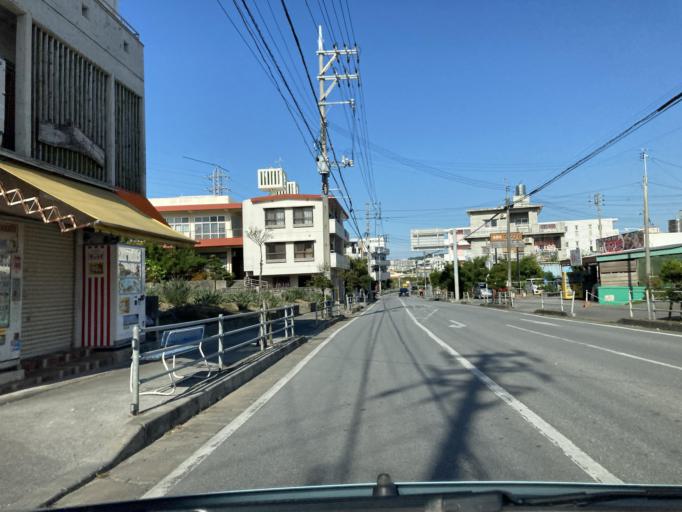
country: JP
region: Okinawa
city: Tomigusuku
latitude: 26.1858
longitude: 127.7079
